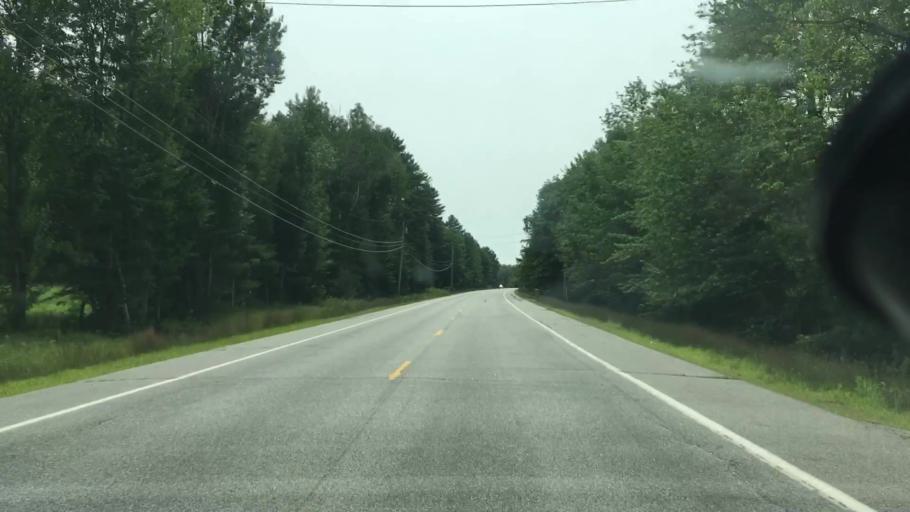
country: US
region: Maine
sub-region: Androscoggin County
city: Livermore Falls
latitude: 44.4340
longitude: -70.1470
